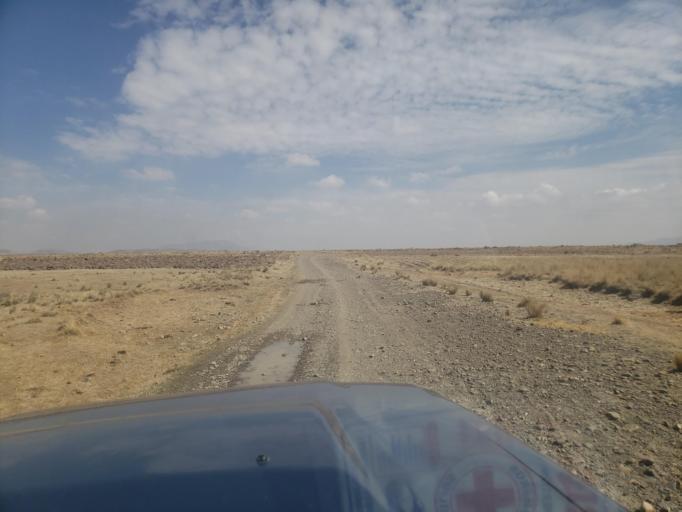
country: BO
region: La Paz
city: Batallas
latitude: -16.4247
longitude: -68.4031
